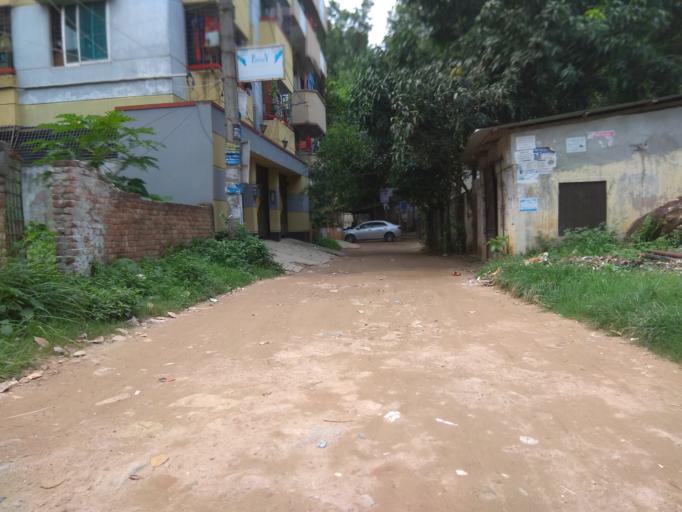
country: BD
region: Dhaka
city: Tungi
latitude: 23.8243
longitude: 90.3517
